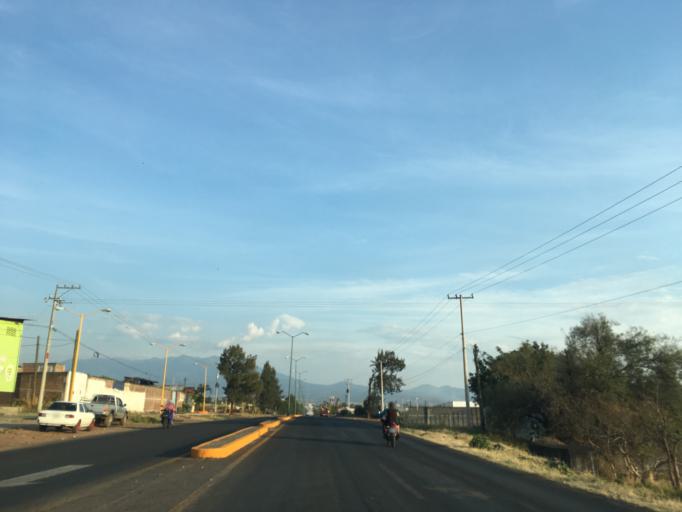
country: MX
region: Michoacan
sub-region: Los Reyes
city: La Higuerita (Colonia San Rafael)
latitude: 19.6122
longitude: -102.4821
